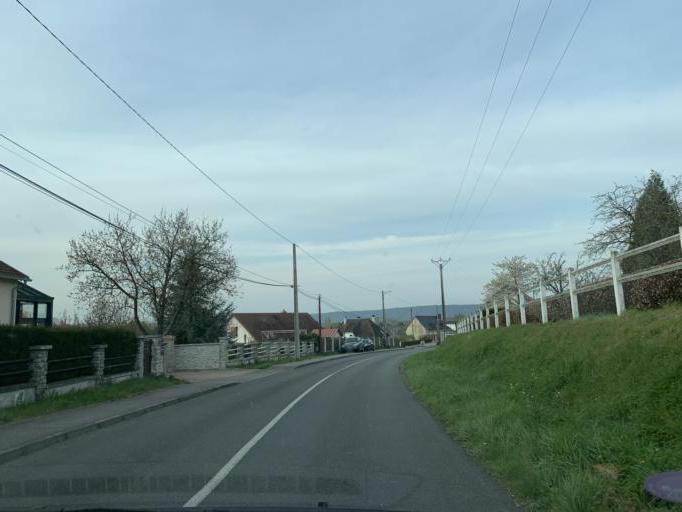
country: FR
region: Haute-Normandie
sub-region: Departement de la Seine-Maritime
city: La Mailleraye-sur-Seine
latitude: 49.4750
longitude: 0.7725
